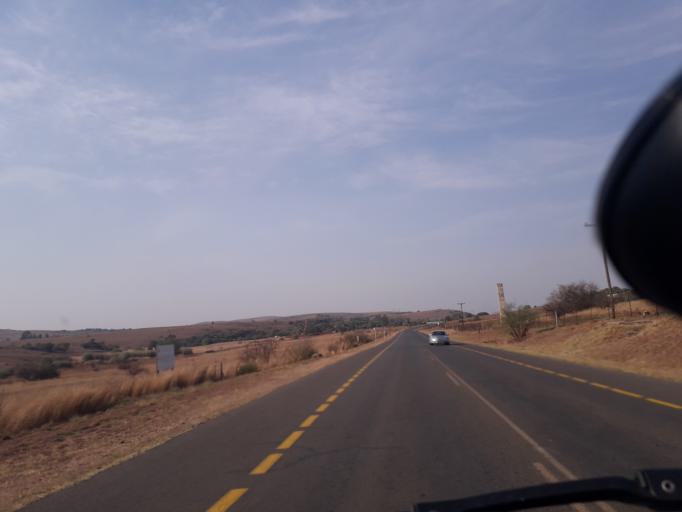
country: ZA
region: Gauteng
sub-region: West Rand District Municipality
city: Krugersdorp
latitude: -26.0188
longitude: 27.7277
